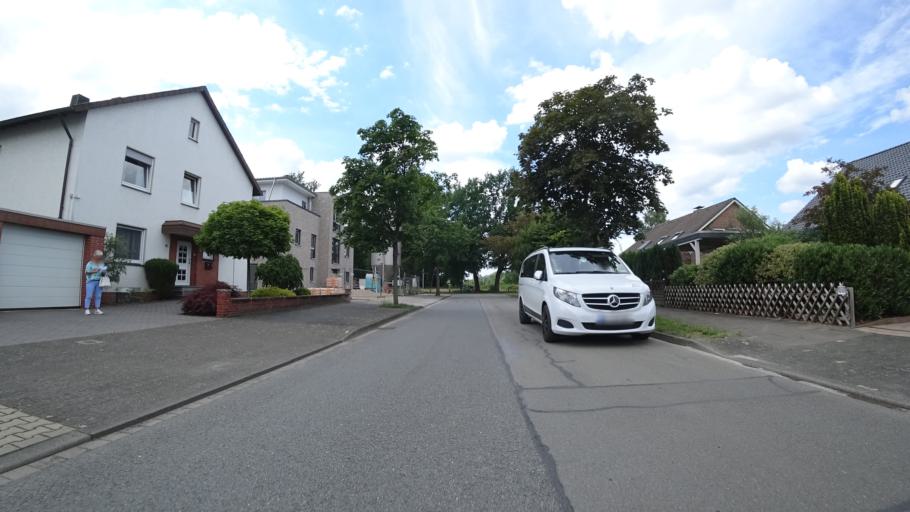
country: DE
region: North Rhine-Westphalia
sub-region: Regierungsbezirk Detmold
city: Guetersloh
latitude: 51.9210
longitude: 8.3813
